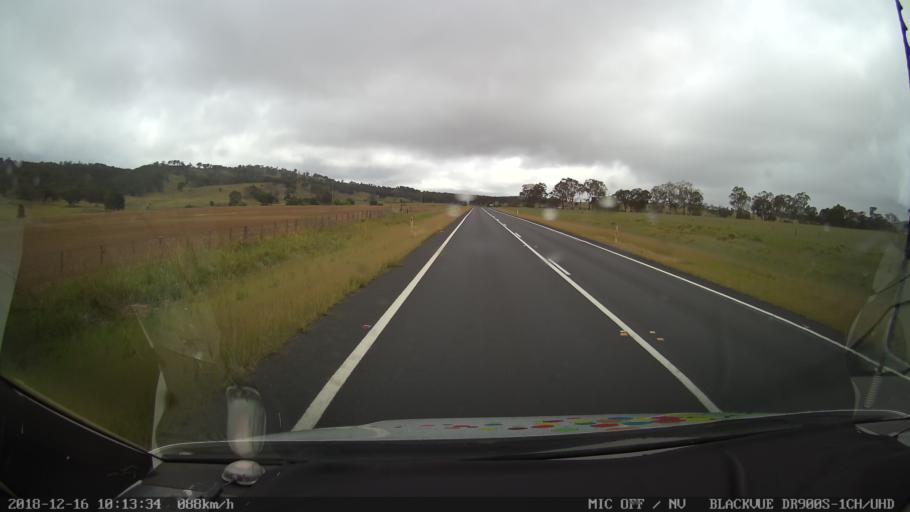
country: AU
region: New South Wales
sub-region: Glen Innes Severn
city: Glen Innes
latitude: -29.2961
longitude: 151.9539
